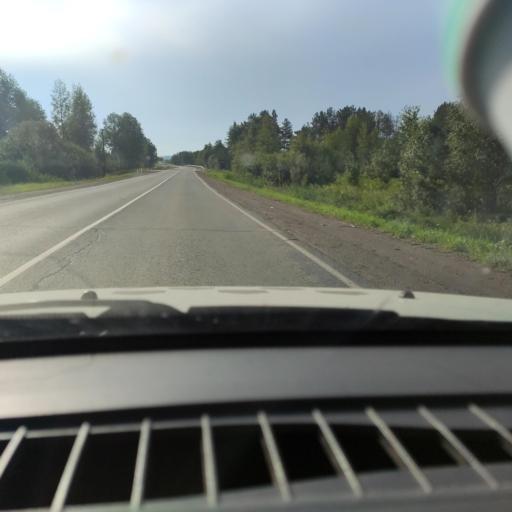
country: RU
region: Kirov
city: Kostino
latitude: 58.8539
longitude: 53.2142
